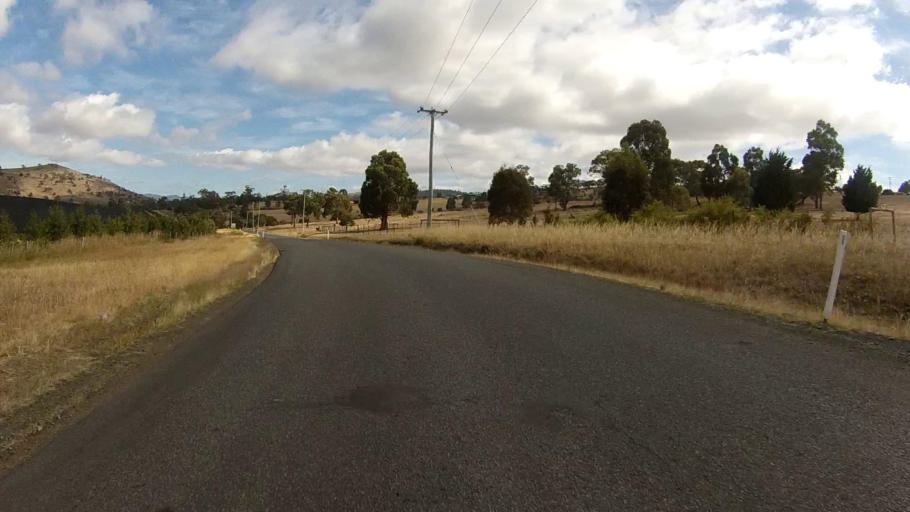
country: AU
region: Tasmania
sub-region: Brighton
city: Old Beach
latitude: -42.7427
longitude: 147.3024
